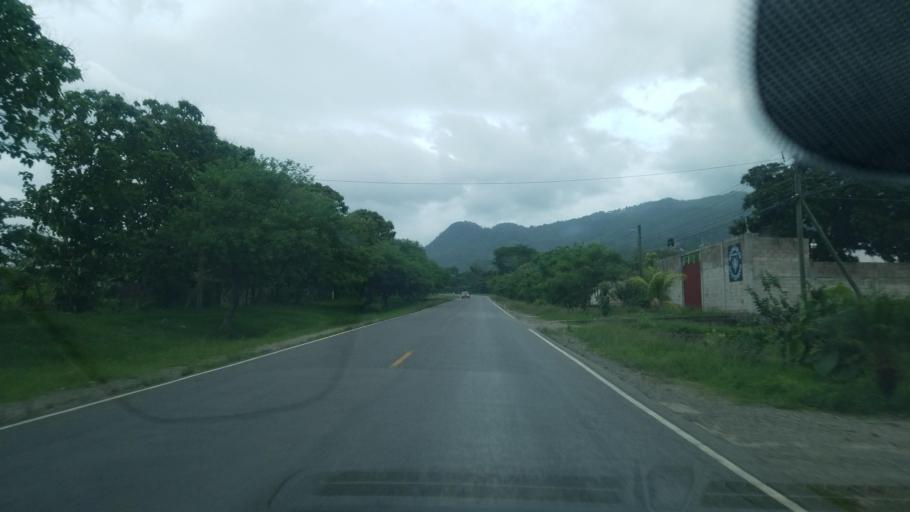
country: HN
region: Ocotepeque
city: Santa Lucia
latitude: 14.4190
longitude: -89.1913
